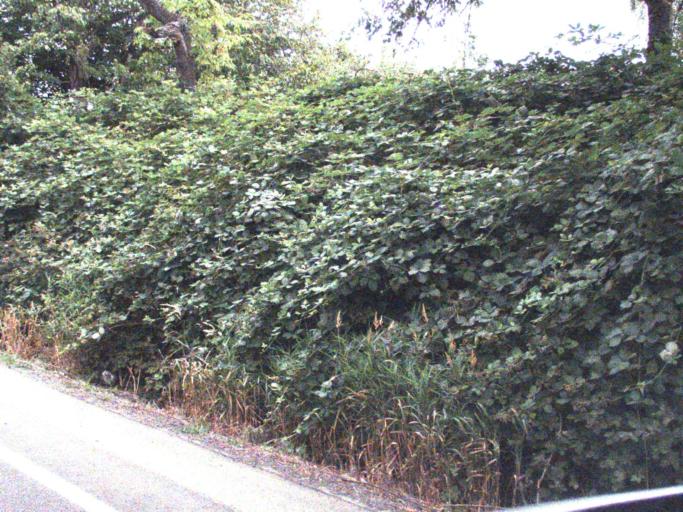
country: US
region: Washington
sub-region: King County
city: Carnation
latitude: 47.6096
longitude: -121.9124
